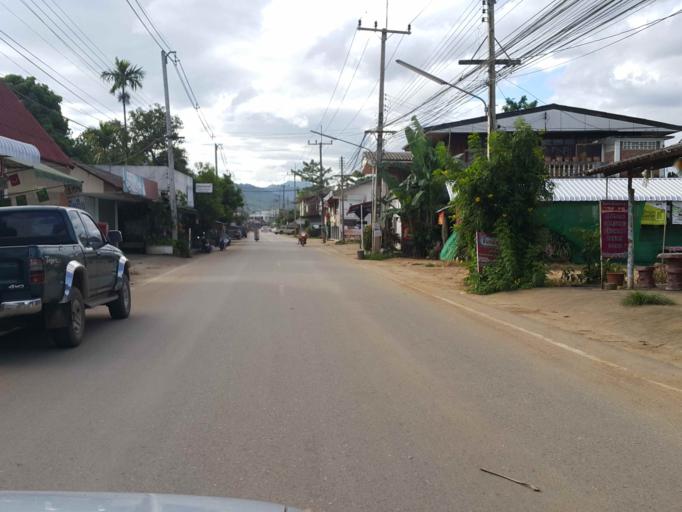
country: TH
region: Chiang Mai
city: Mae Chaem
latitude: 18.5012
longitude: 98.3619
